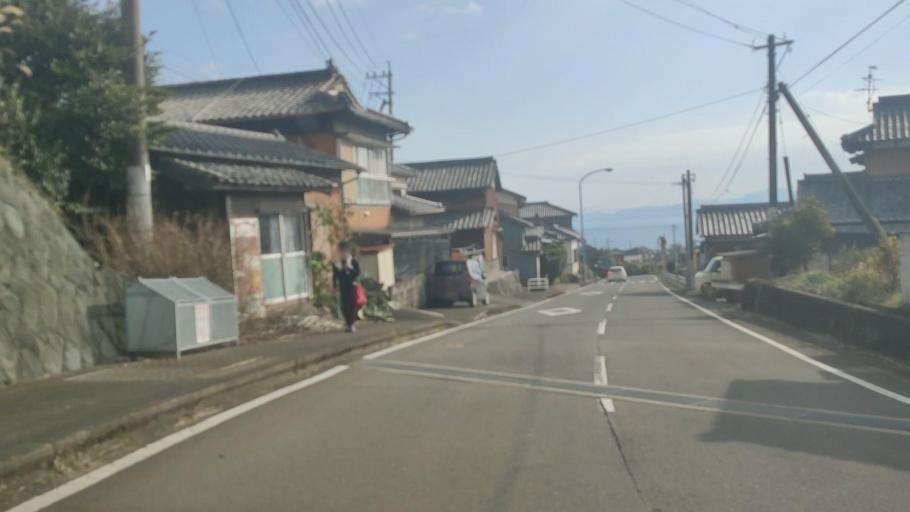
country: JP
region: Nagasaki
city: Shimabara
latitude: 32.6773
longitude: 130.2803
